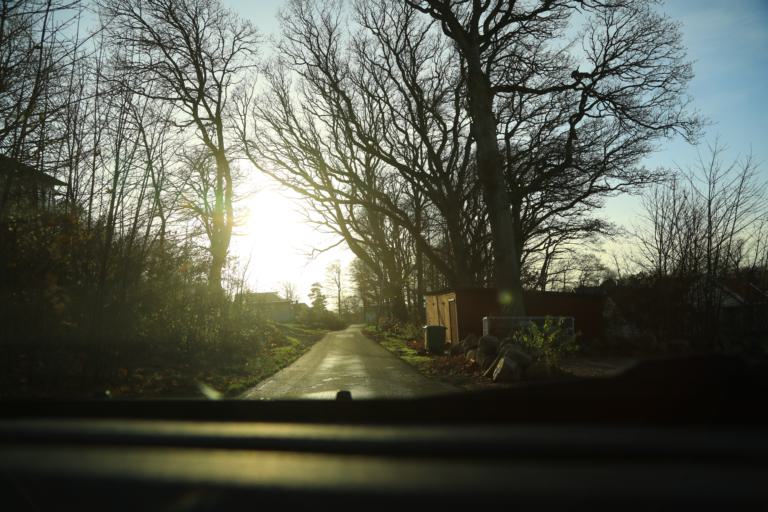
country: SE
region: Halland
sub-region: Varbergs Kommun
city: Varberg
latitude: 57.1902
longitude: 12.2141
